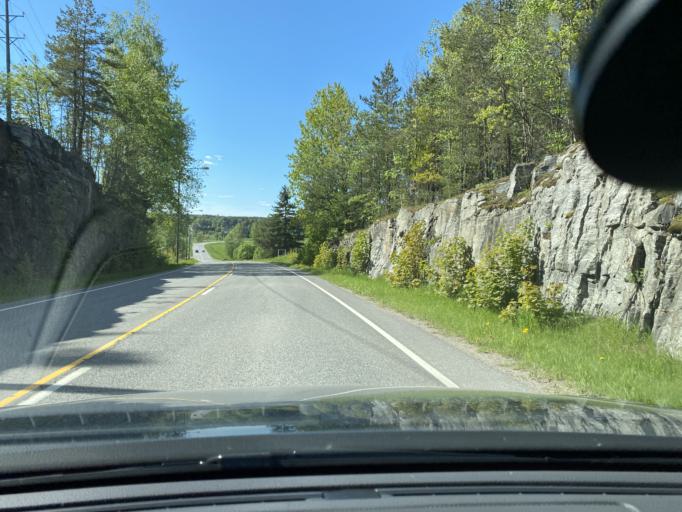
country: FI
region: Varsinais-Suomi
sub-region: Turku
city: Sauvo
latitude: 60.3496
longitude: 22.6798
